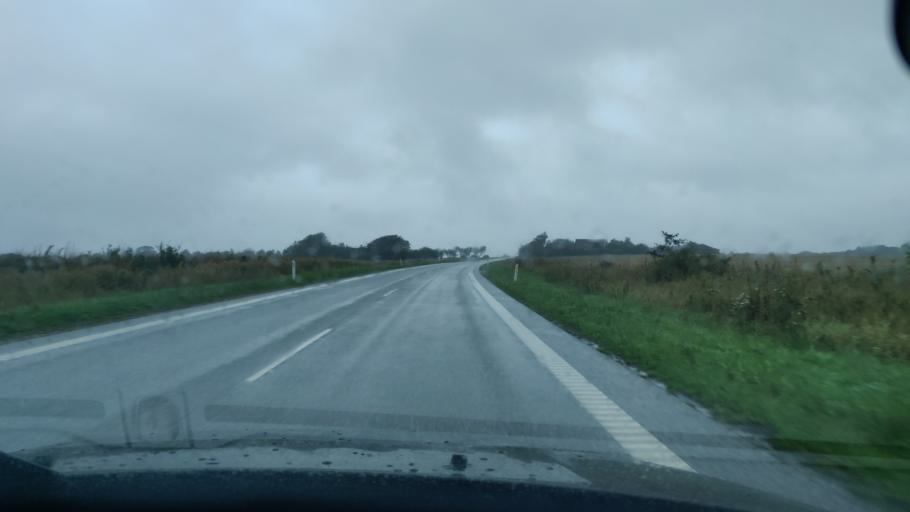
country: DK
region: North Denmark
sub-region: Thisted Kommune
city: Hurup
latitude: 56.8561
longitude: 8.5456
